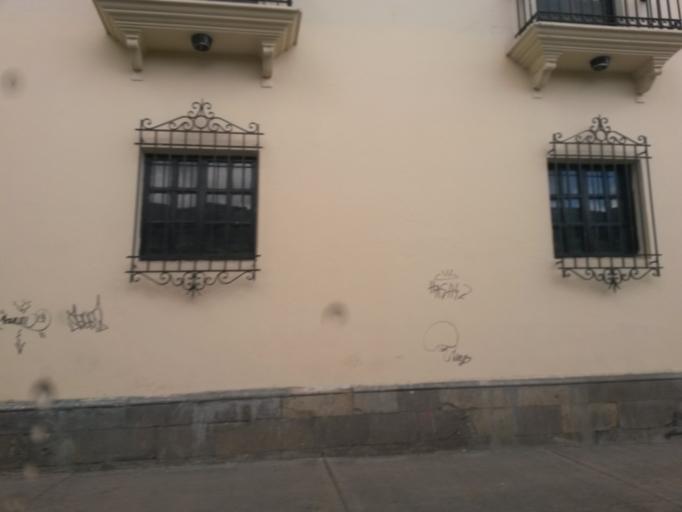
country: CO
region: Cauca
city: Popayan
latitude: 2.4420
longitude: -76.6028
